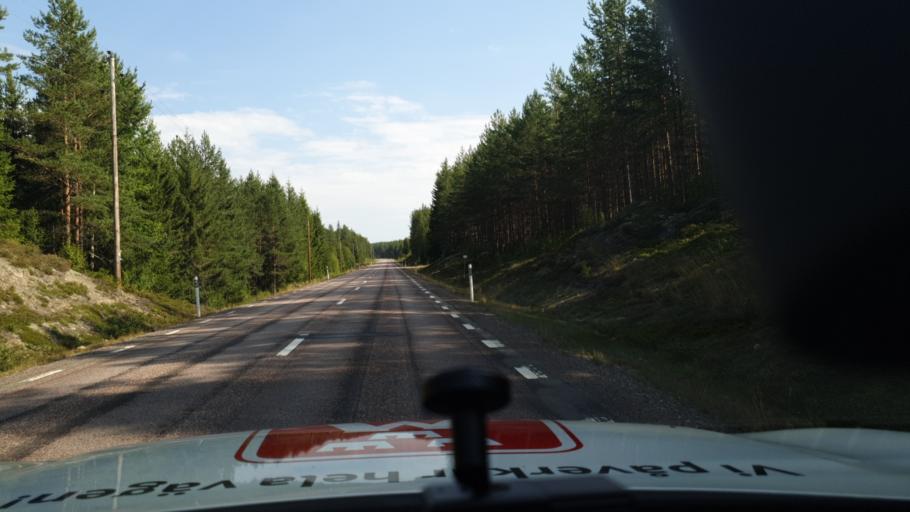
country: SE
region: Vaermland
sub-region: Hagfors Kommun
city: Ekshaerad
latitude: 60.4452
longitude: 13.2764
